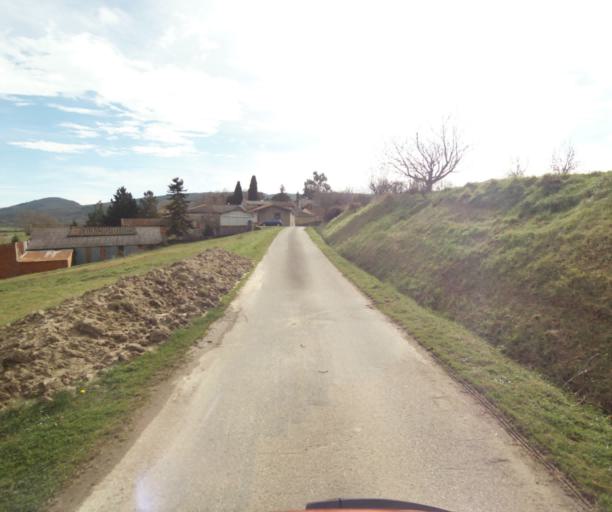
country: FR
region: Midi-Pyrenees
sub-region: Departement de l'Ariege
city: Verniolle
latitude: 43.0621
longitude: 1.7381
